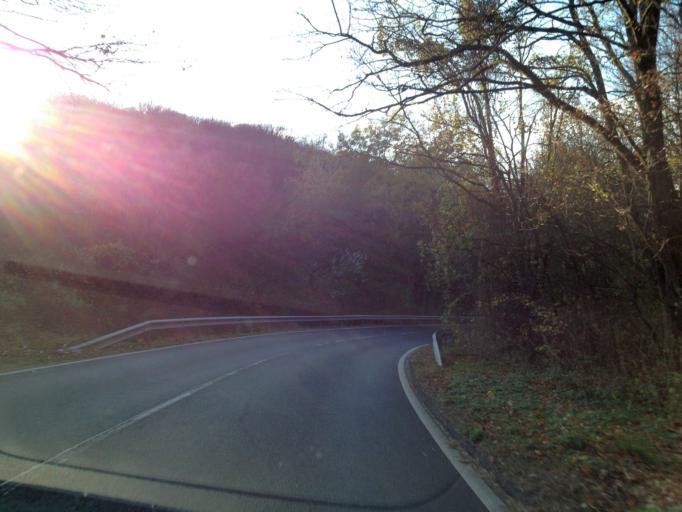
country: HU
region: Veszprem
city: Zirc
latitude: 47.3410
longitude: 17.8802
